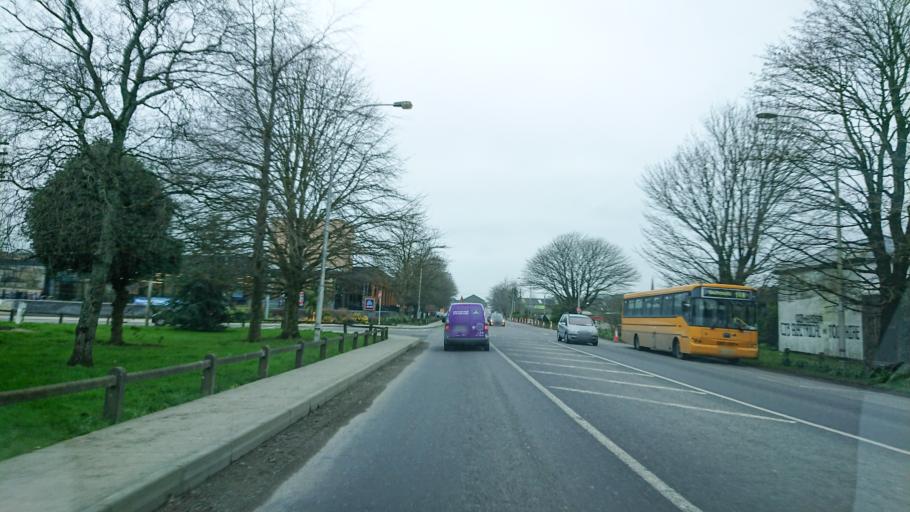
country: IE
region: Munster
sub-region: County Cork
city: Bandon
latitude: 51.7463
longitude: -8.7290
